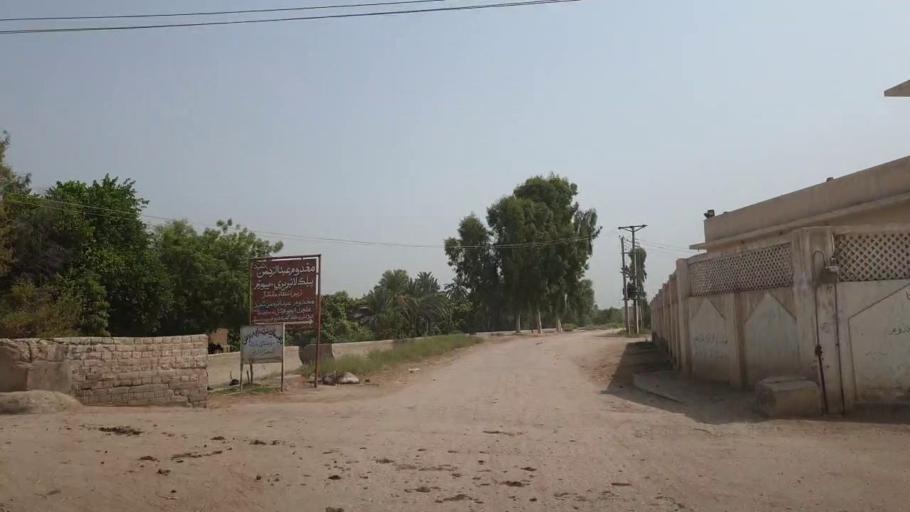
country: PK
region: Sindh
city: Gambat
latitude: 27.3805
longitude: 68.5127
